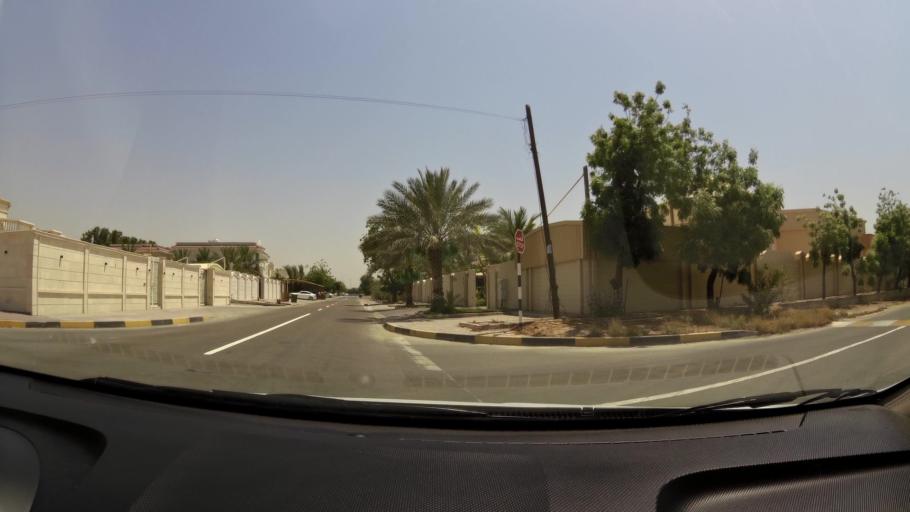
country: AE
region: Ajman
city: Ajman
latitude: 25.4285
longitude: 55.5081
